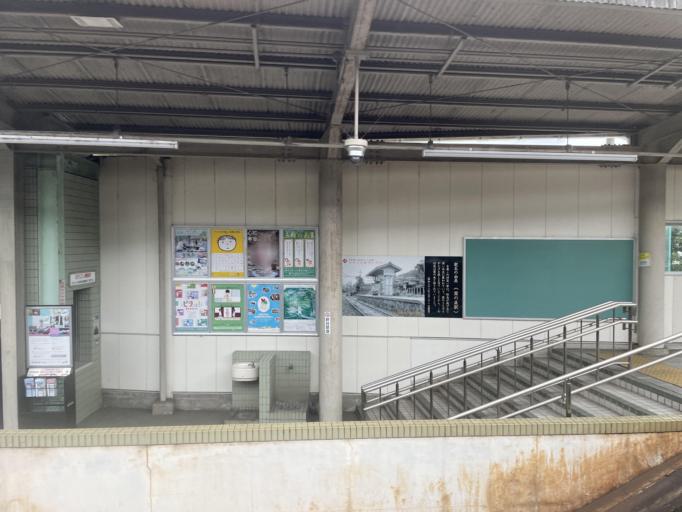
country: JP
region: Osaka
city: Ikeda
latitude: 34.8480
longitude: 135.4189
